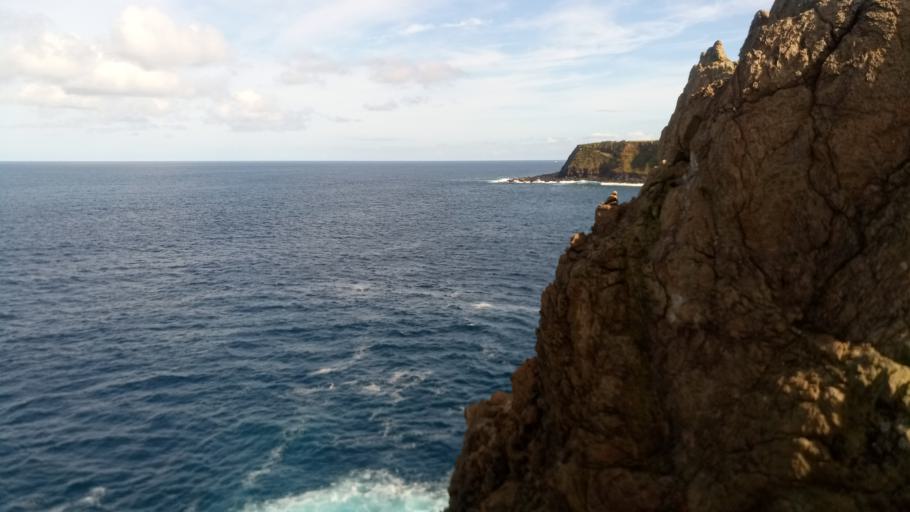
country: PT
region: Azores
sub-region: Praia da Vitoria
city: Biscoitos
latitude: 38.7970
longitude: -27.1920
